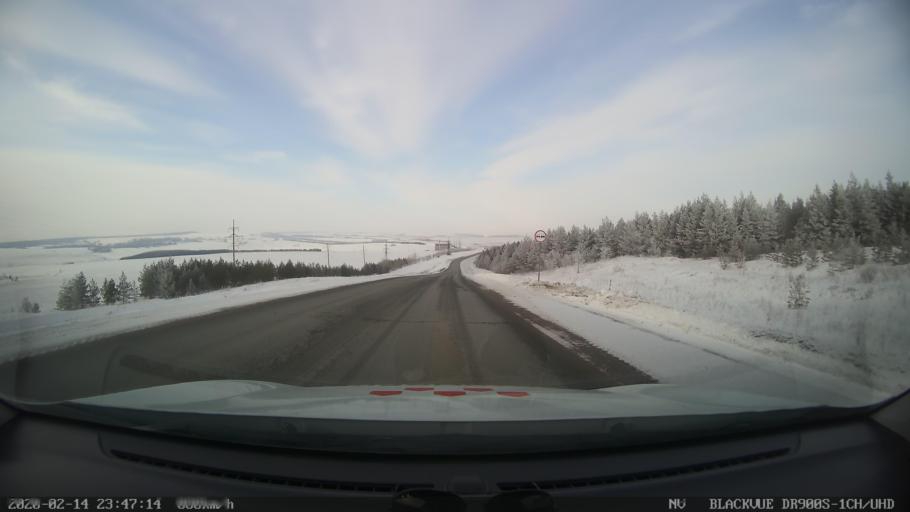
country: RU
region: Tatarstan
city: Kuybyshevskiy Zaton
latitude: 55.2362
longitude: 49.2109
